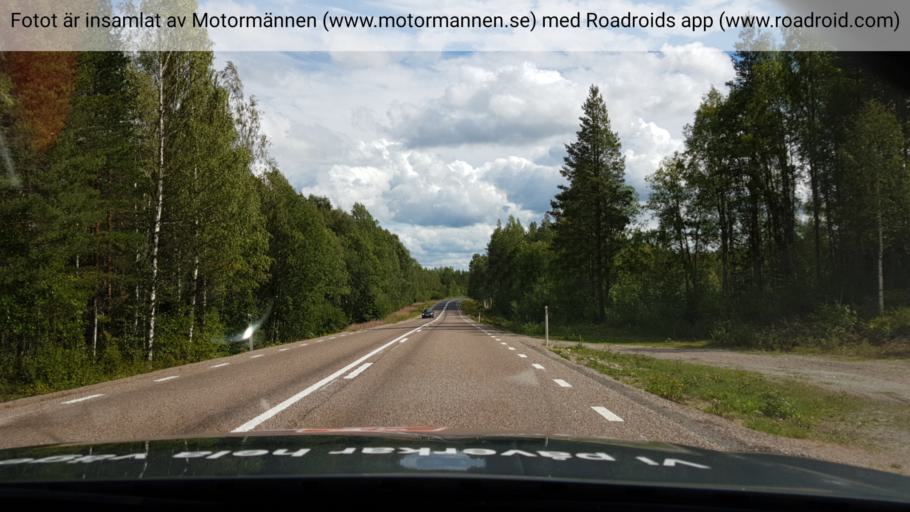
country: SE
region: Jaemtland
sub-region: OEstersunds Kommun
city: Brunflo
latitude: 63.1938
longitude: 15.1566
